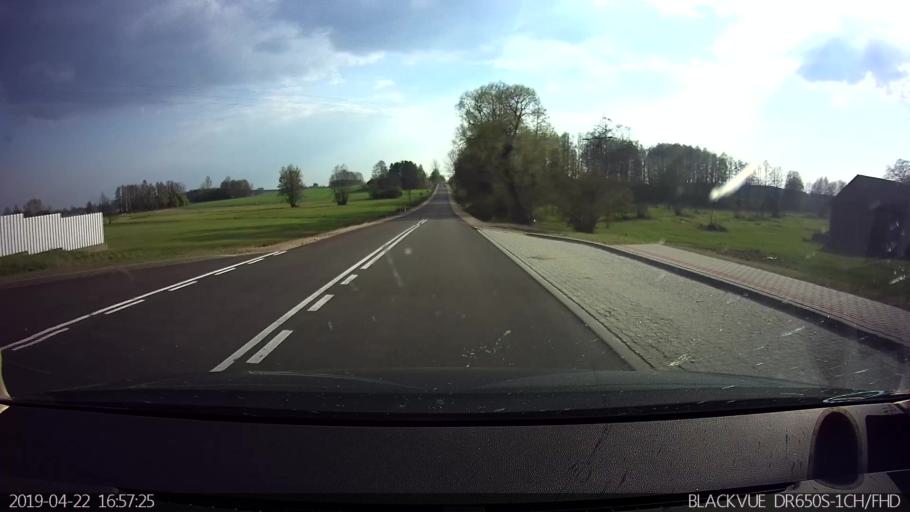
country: PL
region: Podlasie
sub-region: Powiat siemiatycki
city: Siemiatycze
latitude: 52.4805
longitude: 22.7598
